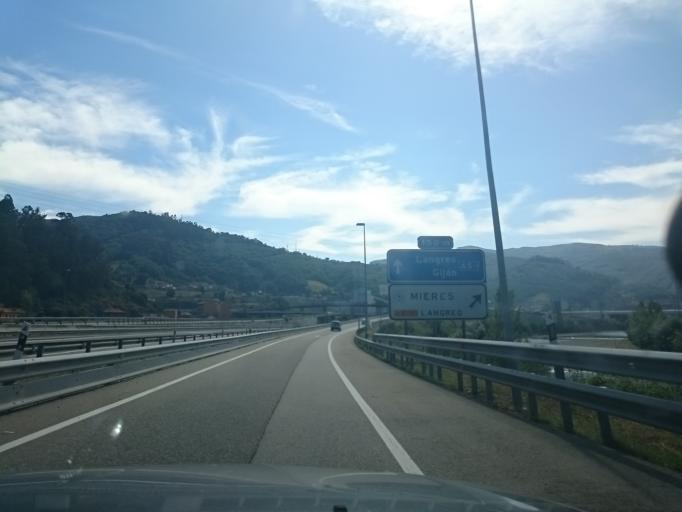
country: ES
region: Asturias
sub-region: Province of Asturias
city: Mieres
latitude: 43.2636
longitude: -5.7875
